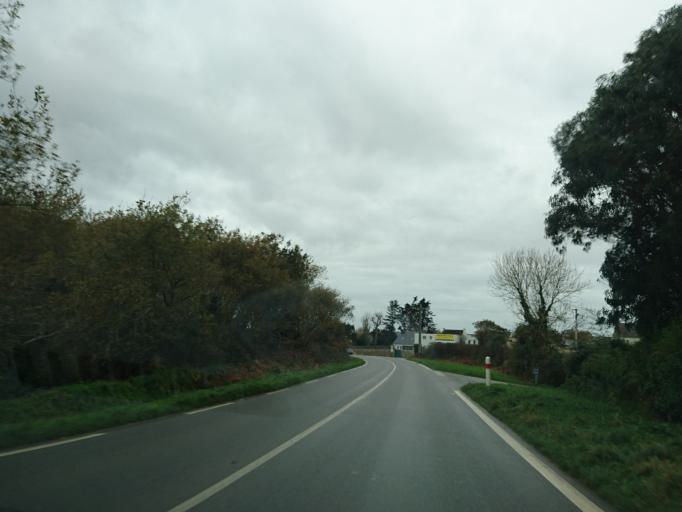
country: FR
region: Brittany
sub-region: Departement du Finistere
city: Plouzane
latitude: 48.3638
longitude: -4.6618
